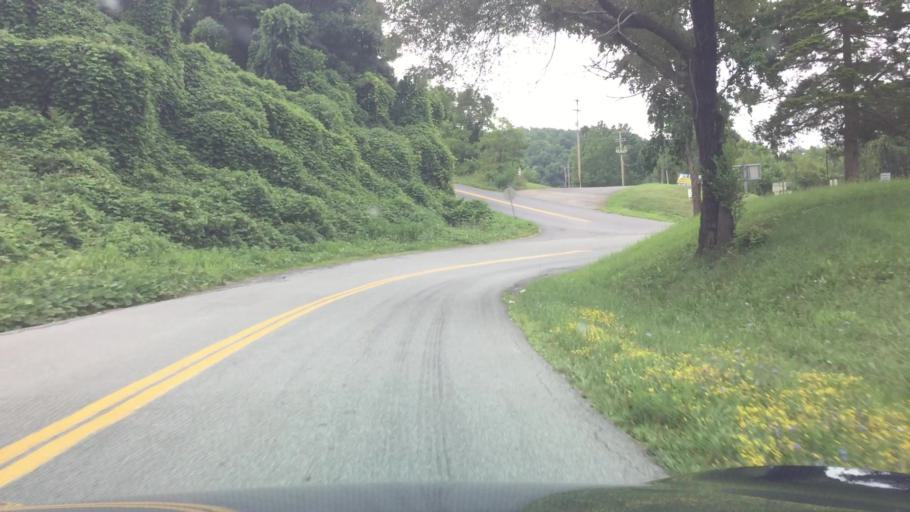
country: US
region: Virginia
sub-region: Pulaski County
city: Pulaski
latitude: 36.9910
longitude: -80.7910
